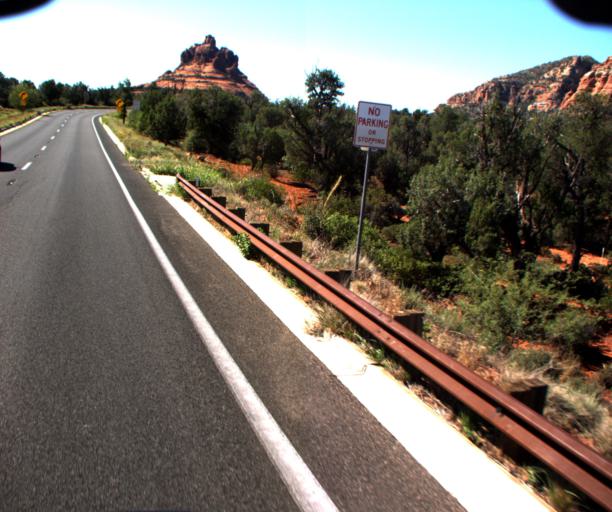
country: US
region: Arizona
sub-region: Yavapai County
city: Village of Oak Creek (Big Park)
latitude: 34.8114
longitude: -111.7687
